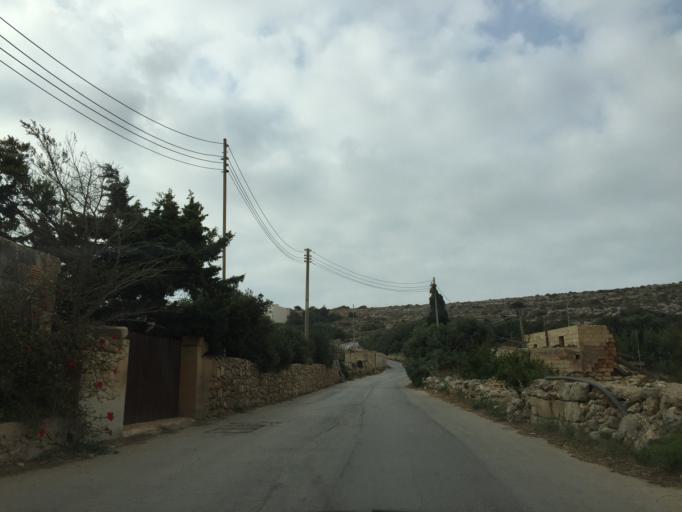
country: MT
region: Il-Mellieha
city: Mellieha
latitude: 35.9382
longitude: 14.3577
